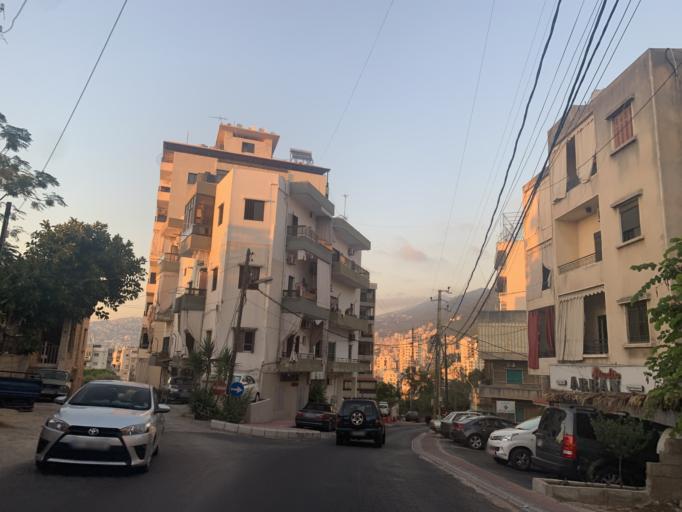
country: LB
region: Mont-Liban
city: Djounie
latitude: 33.9731
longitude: 35.6275
